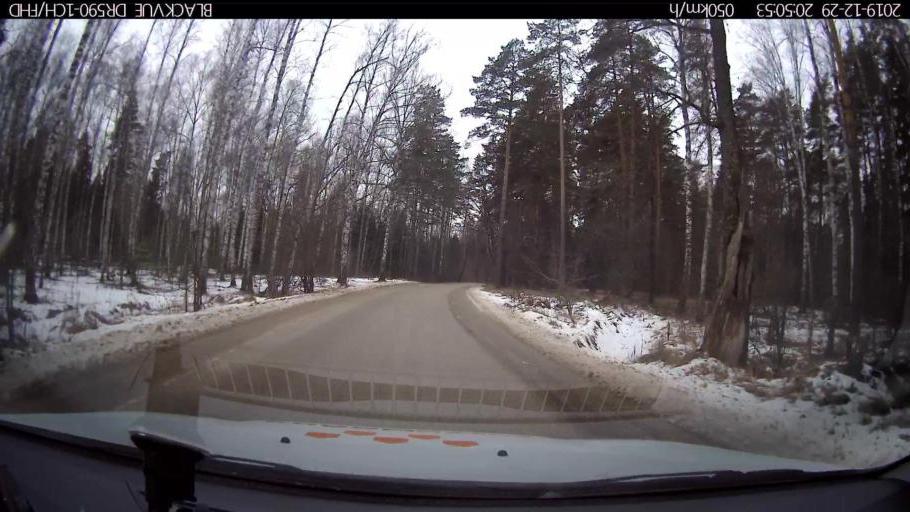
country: RU
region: Nizjnij Novgorod
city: Afonino
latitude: 56.1789
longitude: 44.0086
